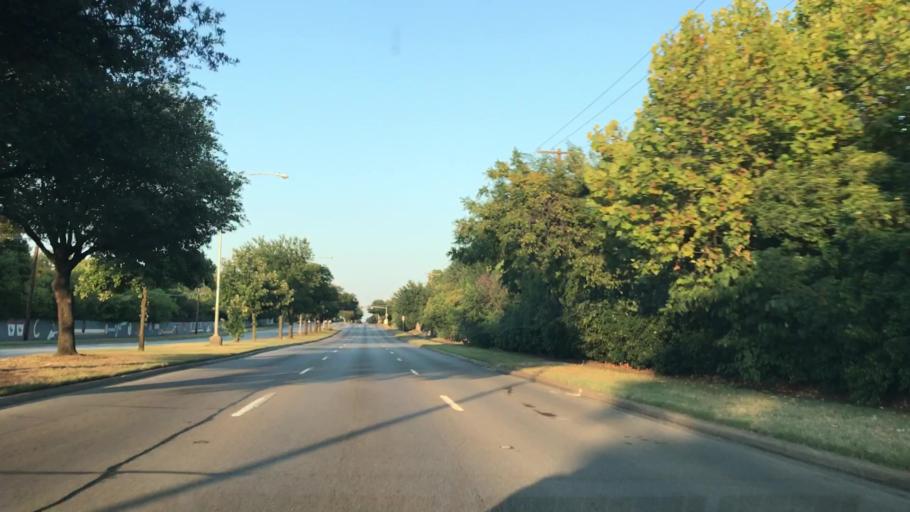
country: US
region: Texas
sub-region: Dallas County
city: Addison
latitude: 32.9095
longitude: -96.8413
